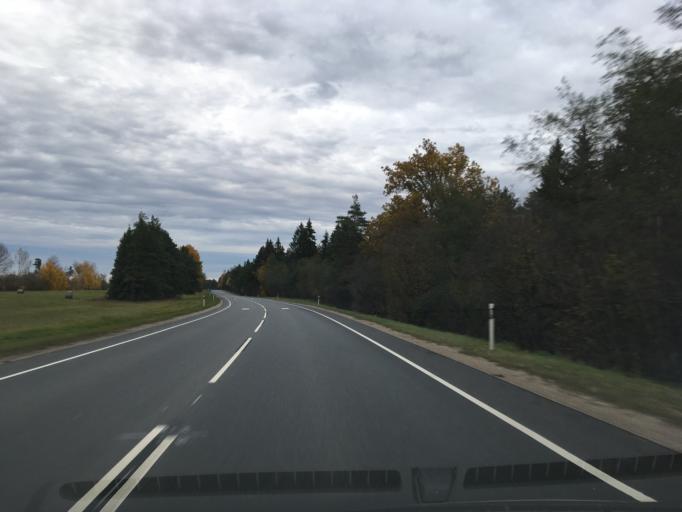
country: EE
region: Harju
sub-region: Nissi vald
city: Turba
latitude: 59.0049
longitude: 24.1233
